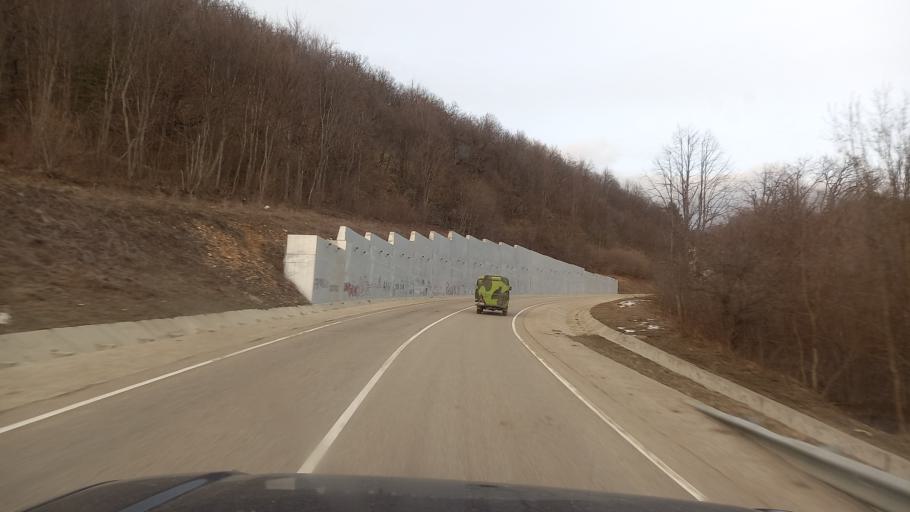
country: RU
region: Adygeya
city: Kamennomostskiy
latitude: 44.2174
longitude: 39.9754
